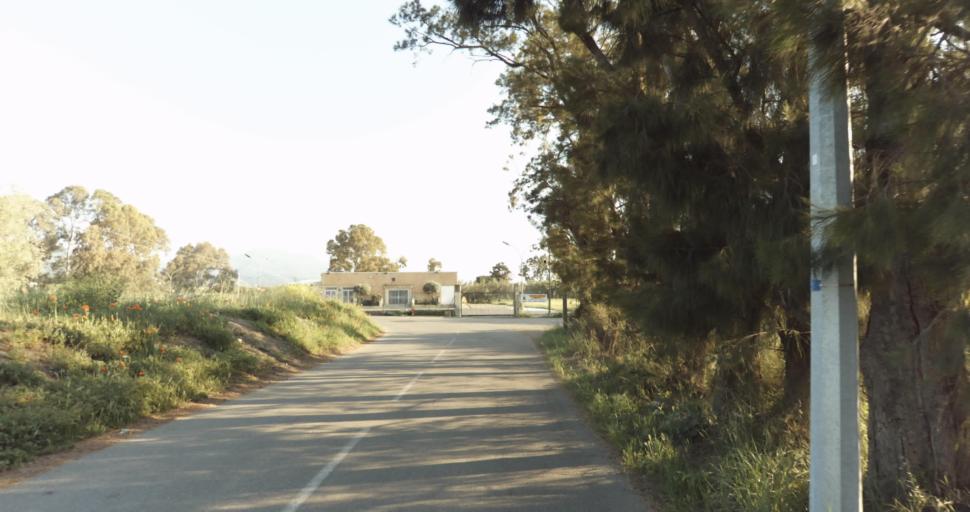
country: FR
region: Corsica
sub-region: Departement de la Haute-Corse
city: Biguglia
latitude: 42.6149
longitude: 9.4440
